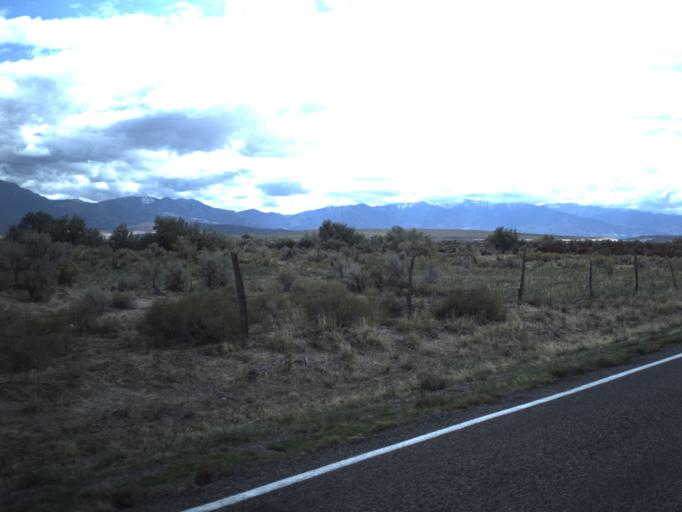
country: US
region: Utah
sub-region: Millard County
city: Fillmore
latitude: 39.1013
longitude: -112.4101
